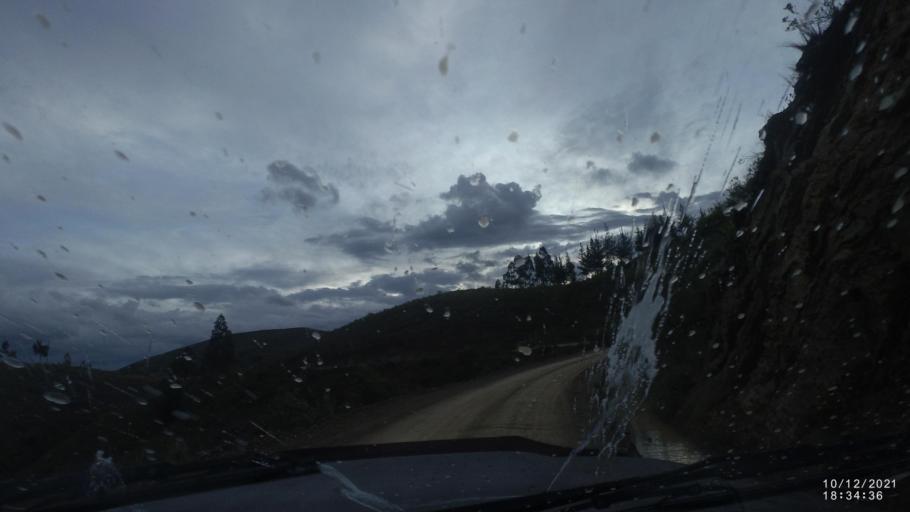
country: BO
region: Cochabamba
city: Tarata
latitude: -17.8237
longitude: -65.9894
